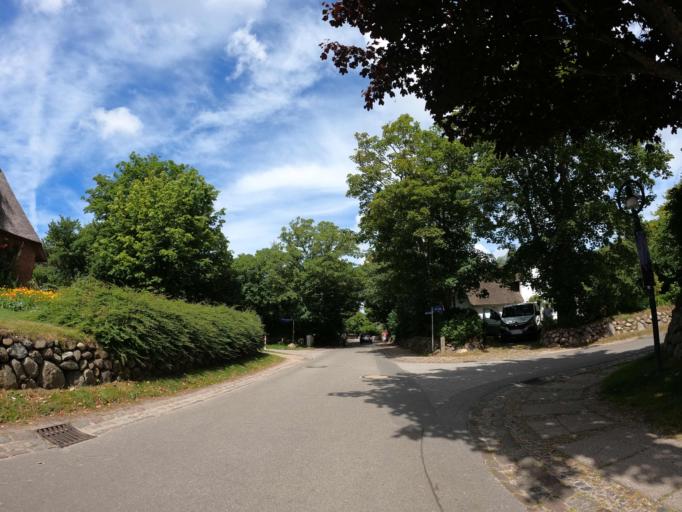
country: DE
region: Schleswig-Holstein
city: Keitum
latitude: 54.8962
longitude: 8.3702
